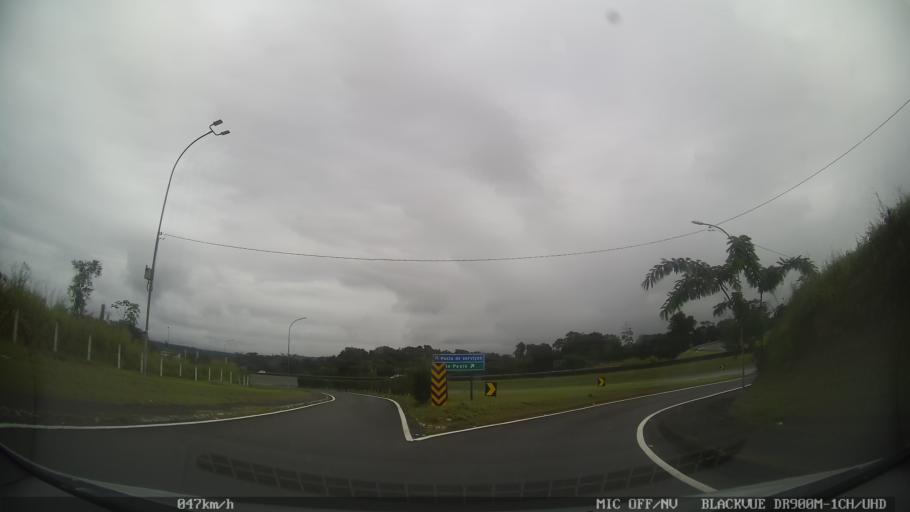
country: BR
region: Sao Paulo
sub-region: Pariquera-Acu
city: Pariquera Acu
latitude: -24.6206
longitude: -47.8925
